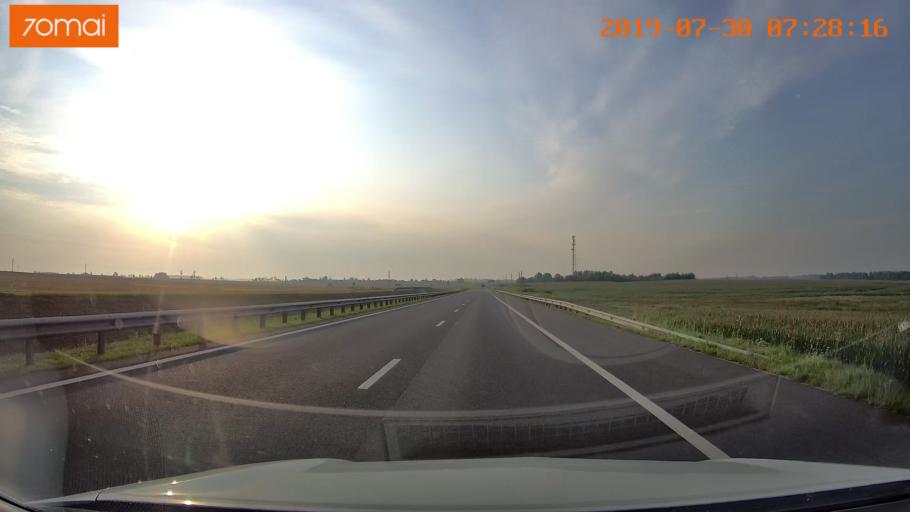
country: RU
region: Kaliningrad
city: Gvardeysk
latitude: 54.6781
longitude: 20.9089
